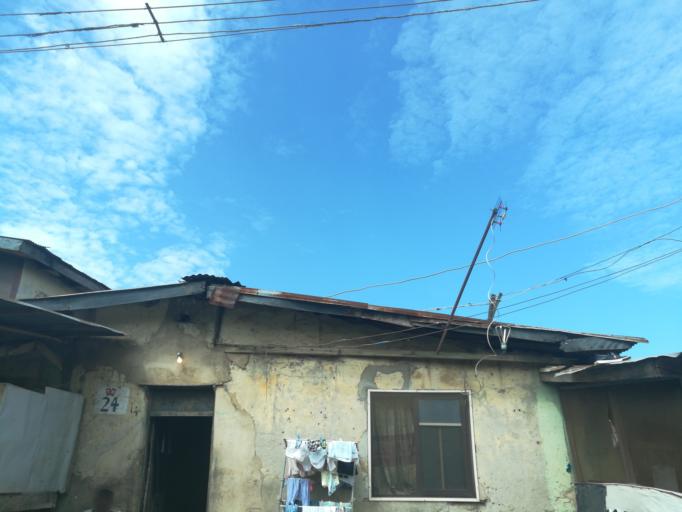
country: NG
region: Lagos
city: Oshodi
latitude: 6.5511
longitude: 3.3350
